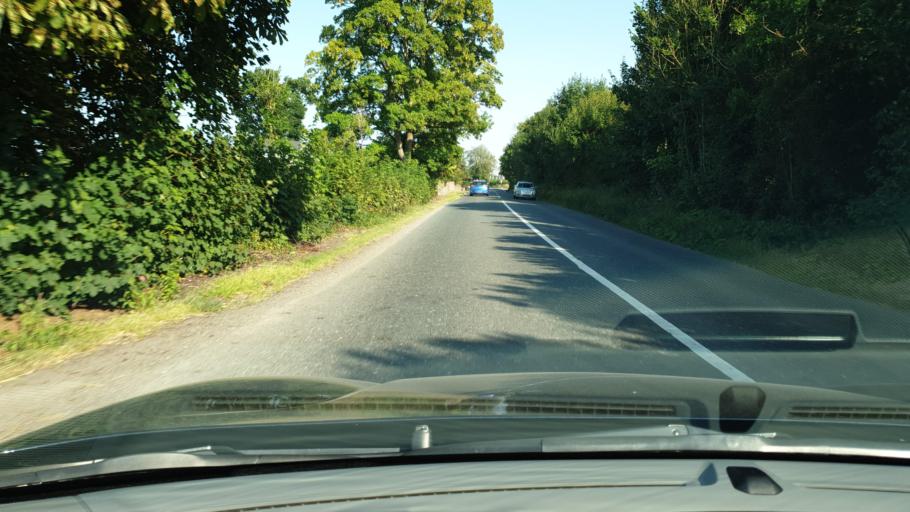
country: IE
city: Kentstown
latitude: 53.6228
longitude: -6.5164
